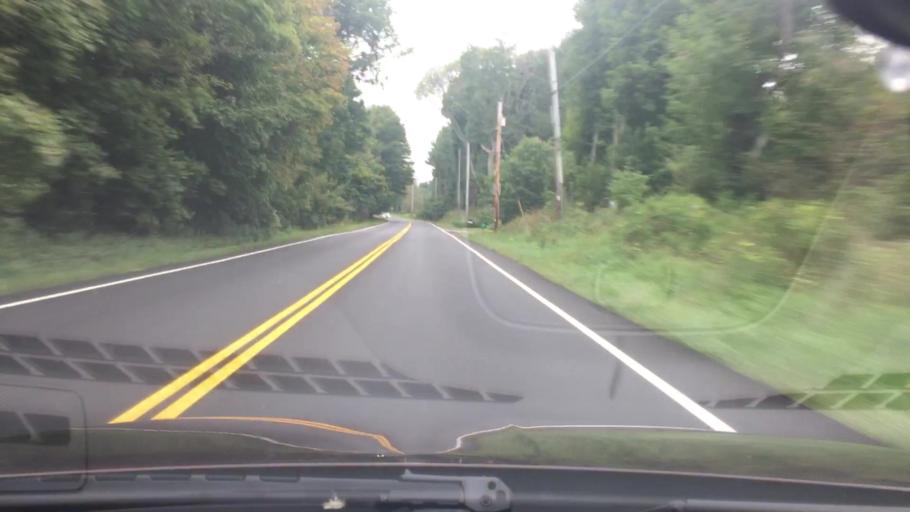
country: US
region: New York
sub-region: Dutchess County
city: Millbrook
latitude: 41.8337
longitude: -73.6150
